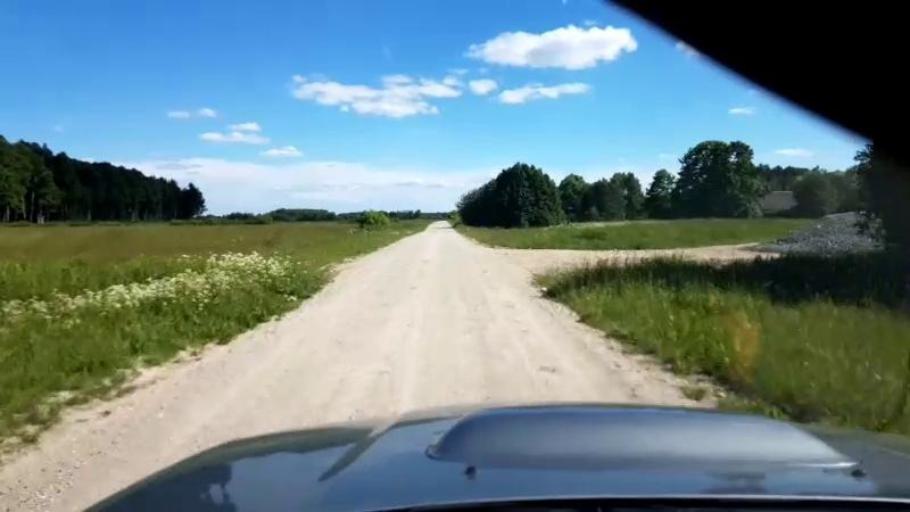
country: EE
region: Paernumaa
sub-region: Sauga vald
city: Sauga
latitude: 58.5062
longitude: 24.5202
